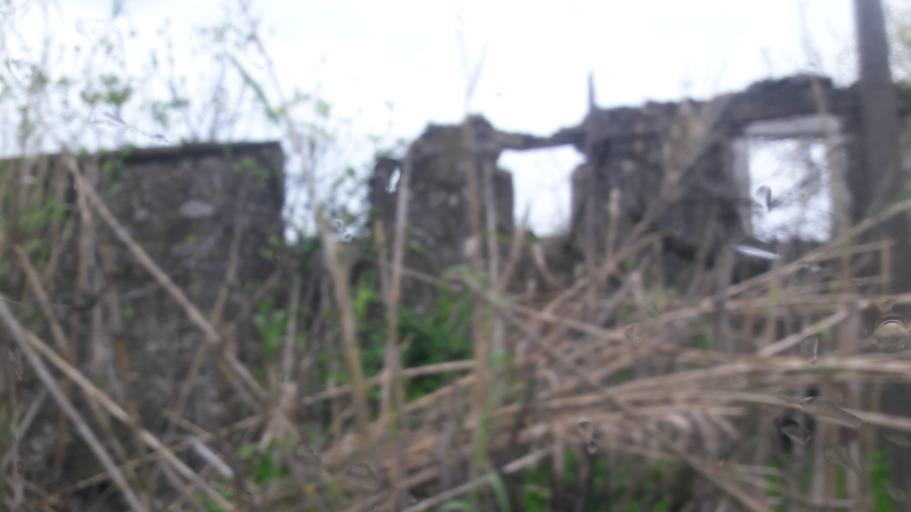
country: AL
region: Shkoder
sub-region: Rrethi i Shkodres
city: Berdica e Madhe
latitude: 41.9552
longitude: 19.5143
